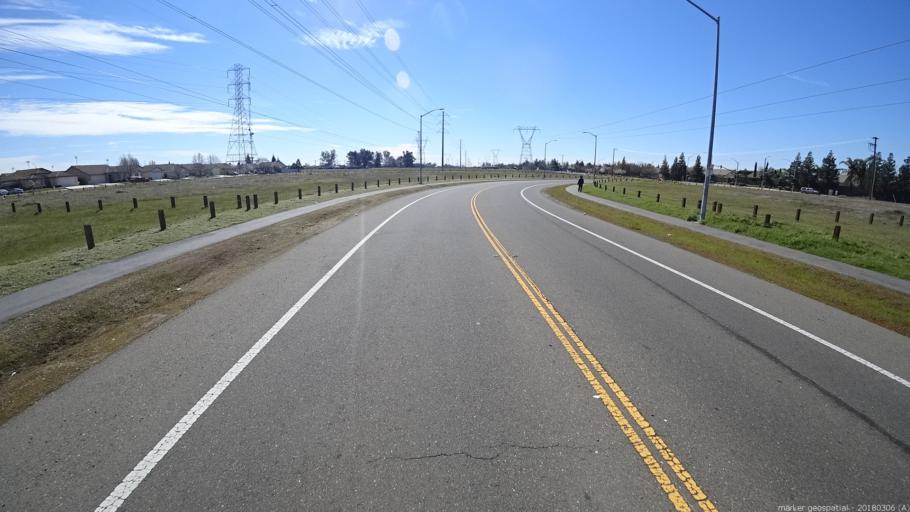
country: US
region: California
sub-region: Sacramento County
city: Vineyard
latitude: 38.4565
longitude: -121.3522
